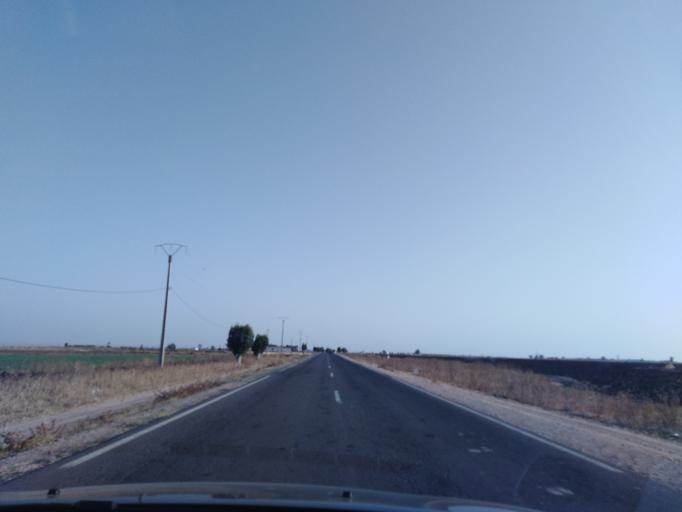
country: MA
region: Doukkala-Abda
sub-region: Safi
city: Youssoufia
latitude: 32.4813
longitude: -8.7690
